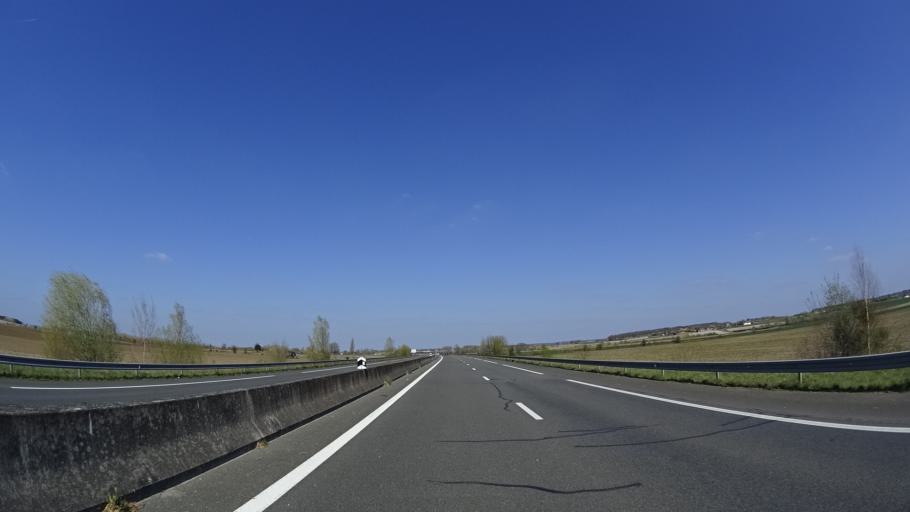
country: FR
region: Pays de la Loire
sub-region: Departement de Maine-et-Loire
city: Saint-Jean
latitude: 47.2626
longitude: -0.3343
